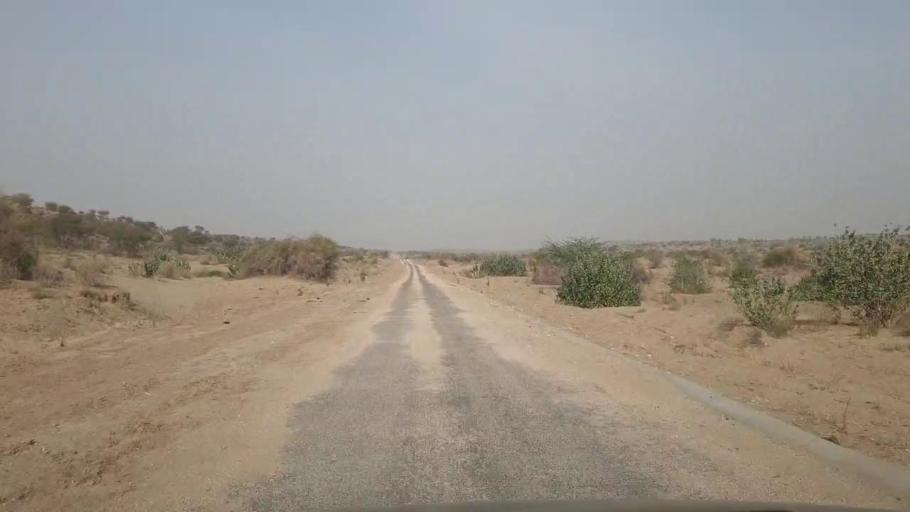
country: PK
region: Sindh
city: Chor
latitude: 25.6266
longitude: 69.9417
